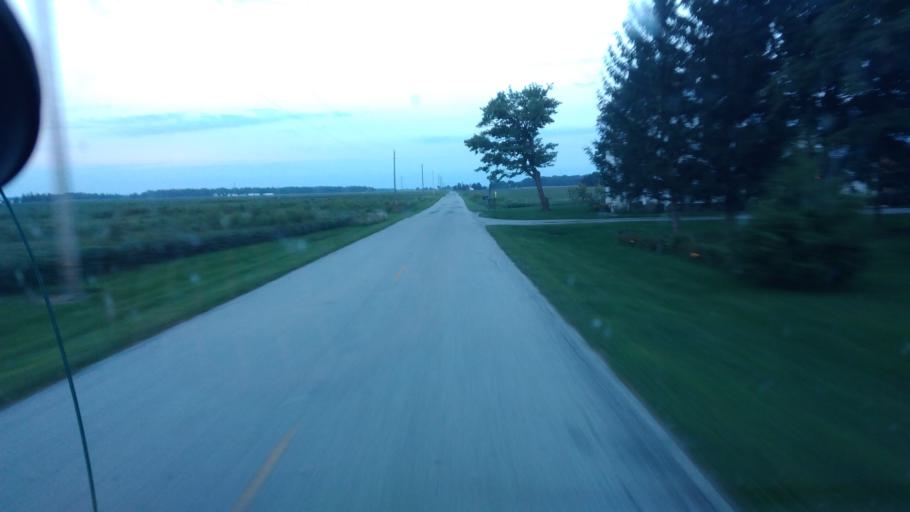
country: US
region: Ohio
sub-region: Hardin County
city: Kenton
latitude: 40.6725
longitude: -83.5191
